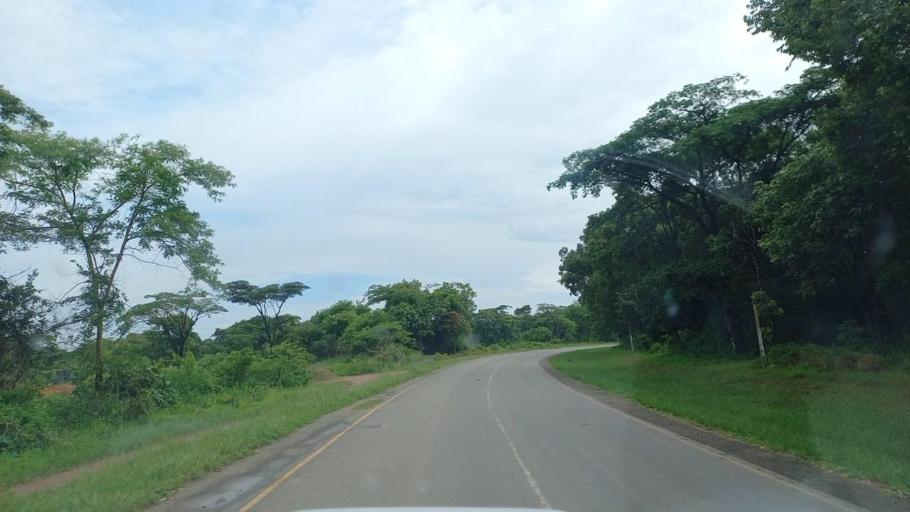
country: ZM
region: Copperbelt
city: Kitwe
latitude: -12.8870
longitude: 28.3113
